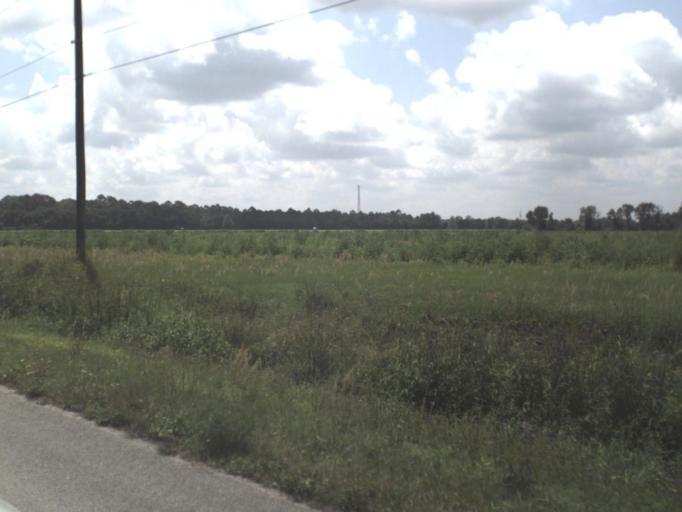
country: US
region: Florida
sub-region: Putnam County
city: East Palatka
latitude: 29.7255
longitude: -81.4700
